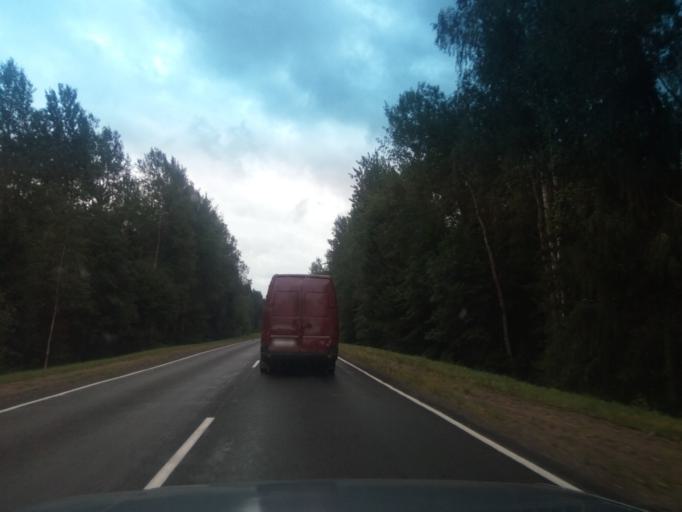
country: BY
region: Vitebsk
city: Polatsk
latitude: 55.4166
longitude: 28.7944
